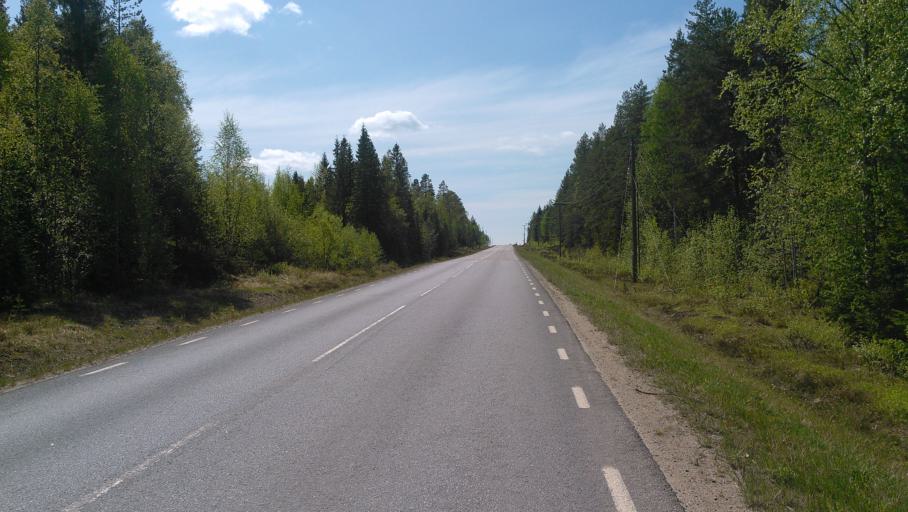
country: SE
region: Vaesterbotten
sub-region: Umea Kommun
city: Roback
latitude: 63.8614
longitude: 20.0085
